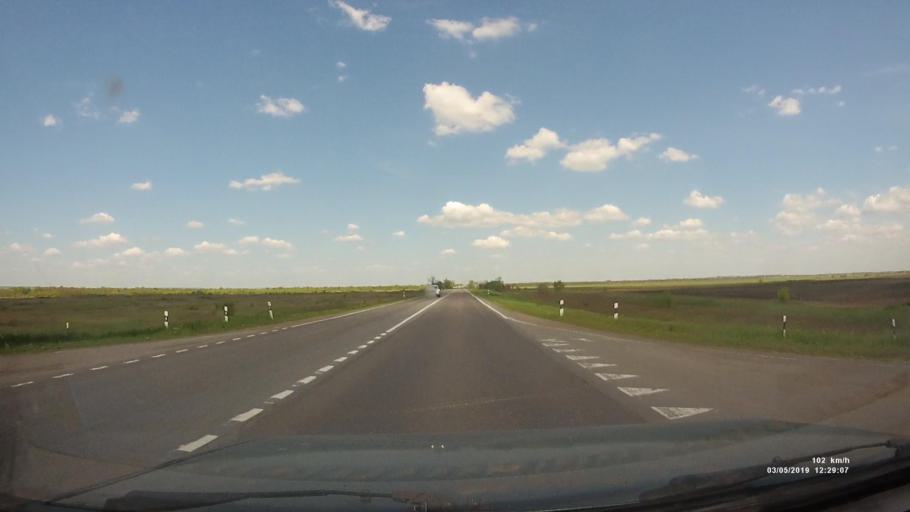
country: RU
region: Rostov
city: Semikarakorsk
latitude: 47.4840
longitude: 40.7360
